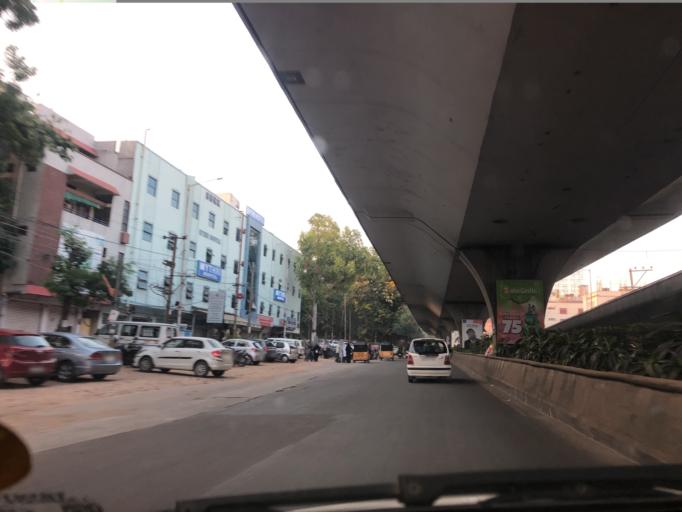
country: IN
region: Telangana
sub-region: Hyderabad
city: Hyderabad
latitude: 17.3832
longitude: 78.4294
